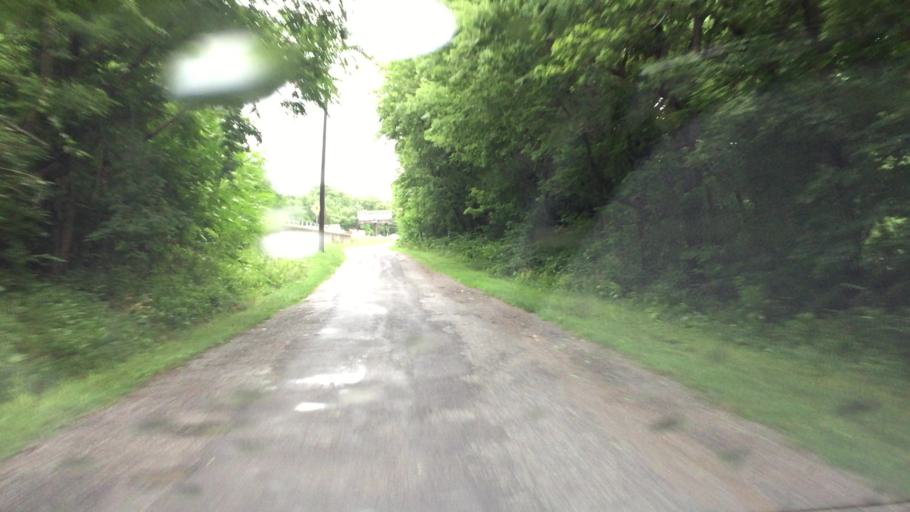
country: US
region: Illinois
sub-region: Hancock County
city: Hamilton
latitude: 40.3945
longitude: -91.3546
